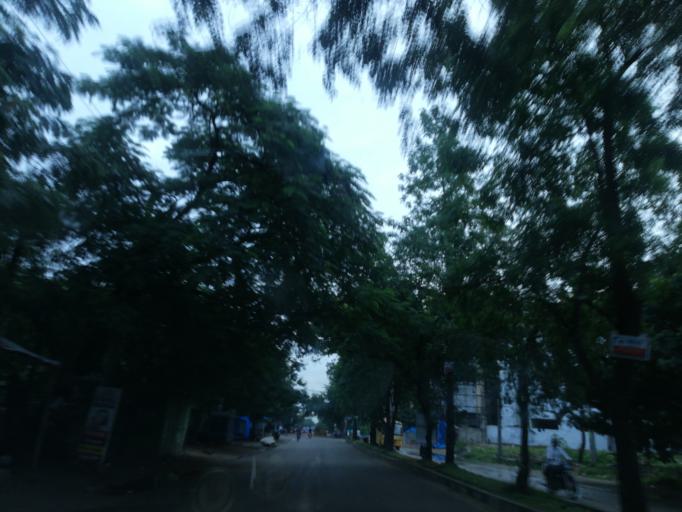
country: IN
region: Telangana
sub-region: Rangareddi
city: Kukatpalli
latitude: 17.4834
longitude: 78.3922
